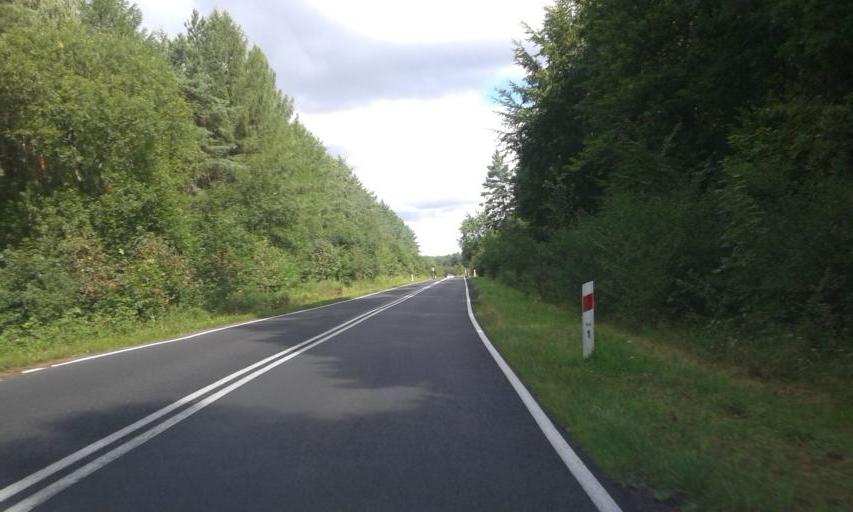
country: PL
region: West Pomeranian Voivodeship
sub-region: Powiat koszalinski
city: Polanow
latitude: 54.0293
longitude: 16.7202
